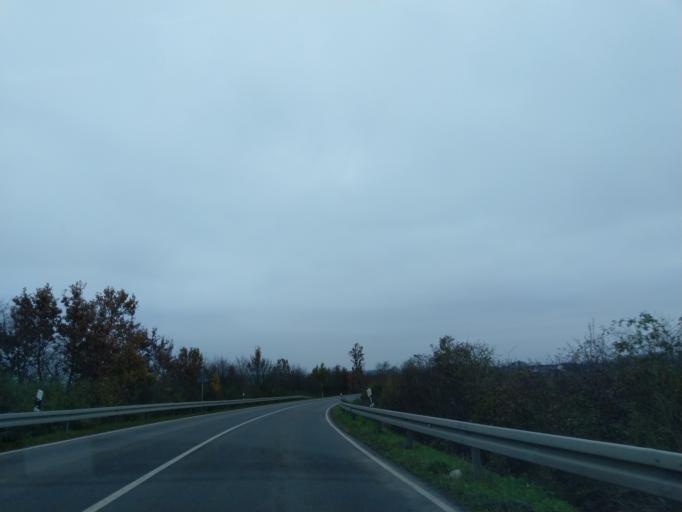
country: DE
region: Bavaria
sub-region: Lower Bavaria
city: Otzing
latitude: 48.7749
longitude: 12.7930
